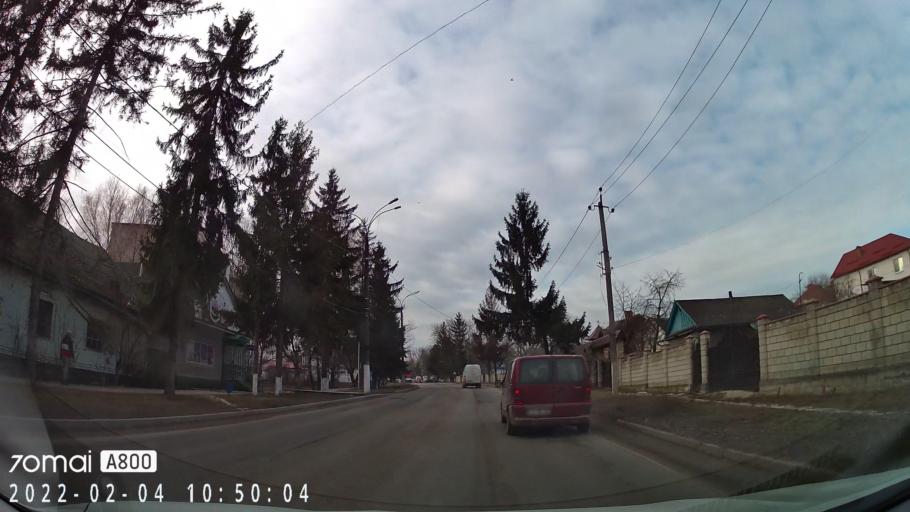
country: MD
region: Briceni
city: Briceni
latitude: 48.3558
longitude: 27.0878
